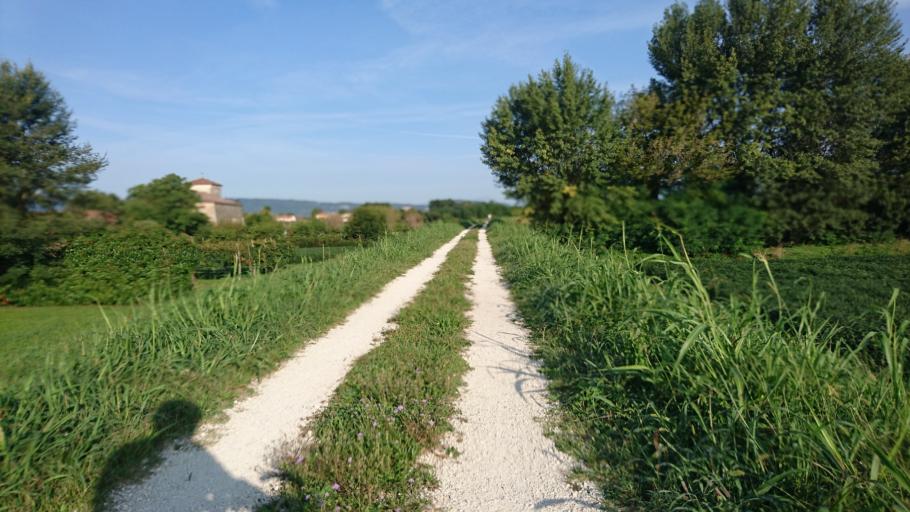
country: IT
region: Veneto
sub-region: Provincia di Padova
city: Cervarese Santa Croce
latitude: 45.4262
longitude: 11.6869
